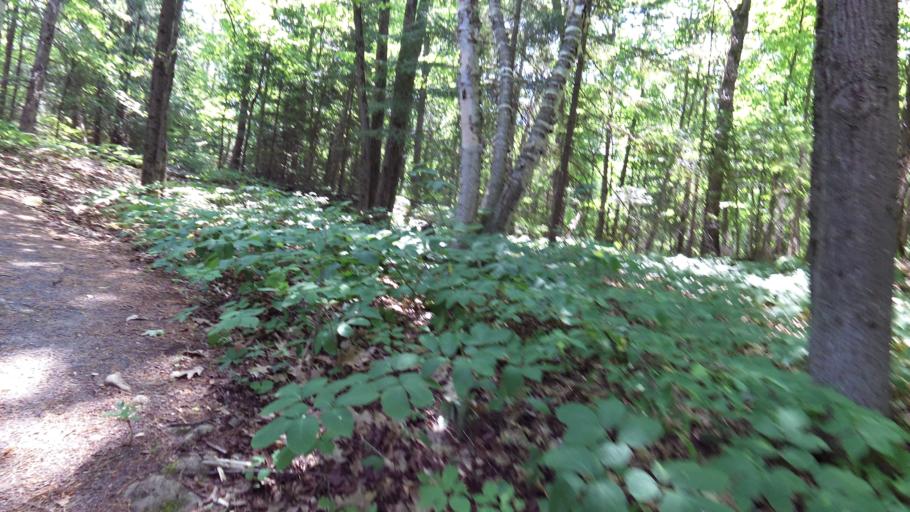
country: CA
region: Ontario
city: Arnprior
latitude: 45.4608
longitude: -76.2584
